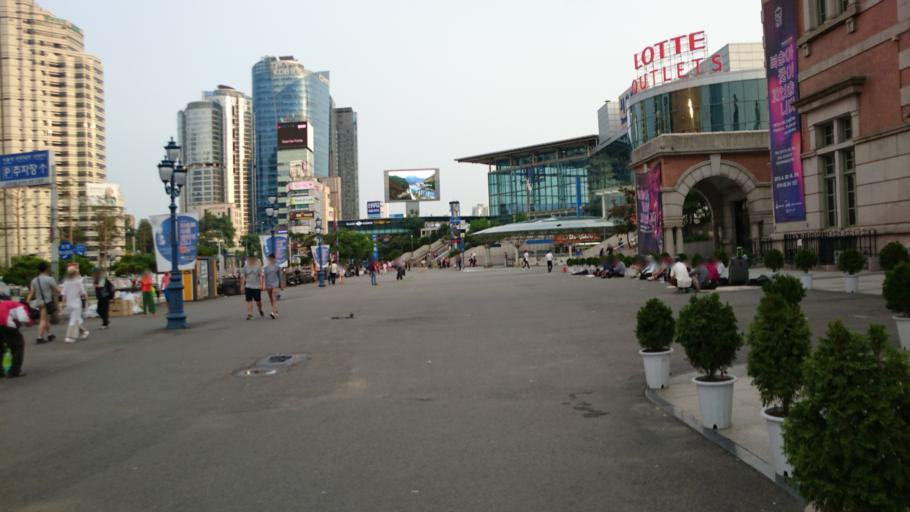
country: KR
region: Seoul
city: Seoul
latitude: 37.5558
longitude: 126.9719
